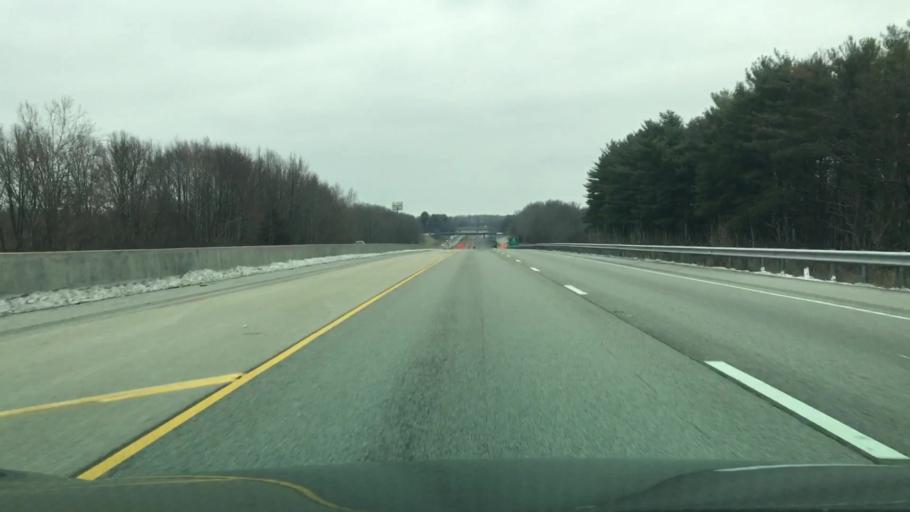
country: US
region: Illinois
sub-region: Franklin County
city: Benton
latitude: 37.9827
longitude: -88.9353
